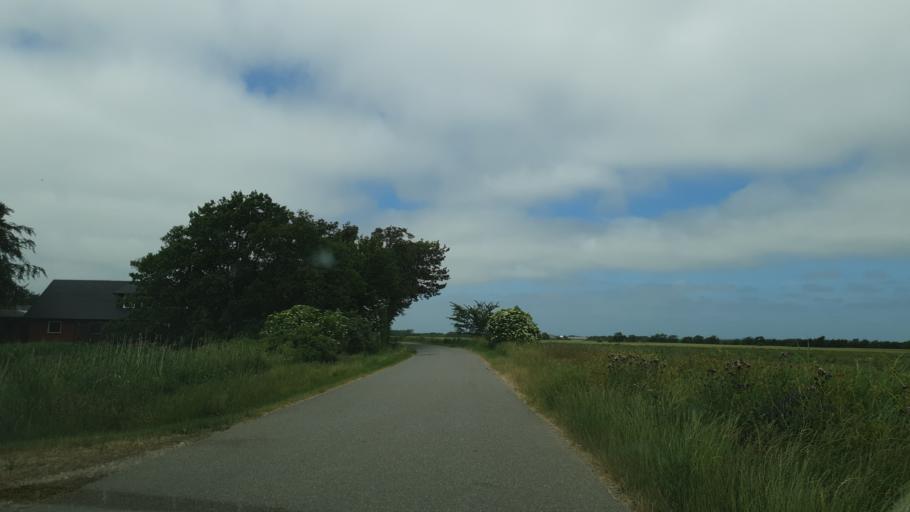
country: DK
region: Central Jutland
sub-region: Ringkobing-Skjern Kommune
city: Skjern
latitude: 55.9333
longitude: 8.4024
